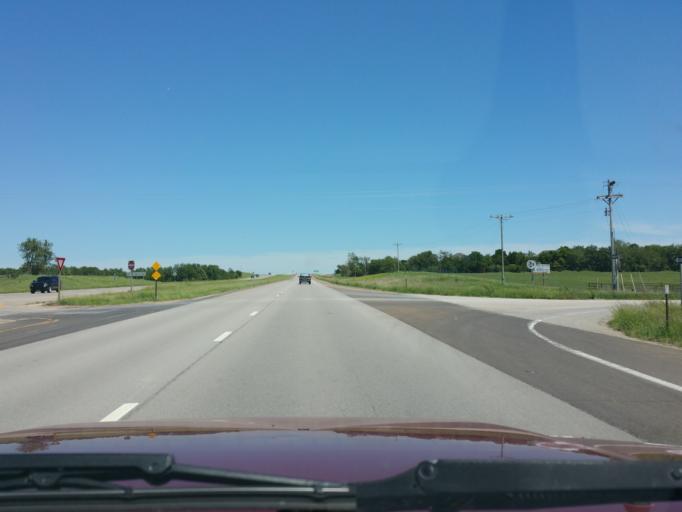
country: US
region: Kansas
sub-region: Pottawatomie County
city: Wamego
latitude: 39.2097
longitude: -96.3990
